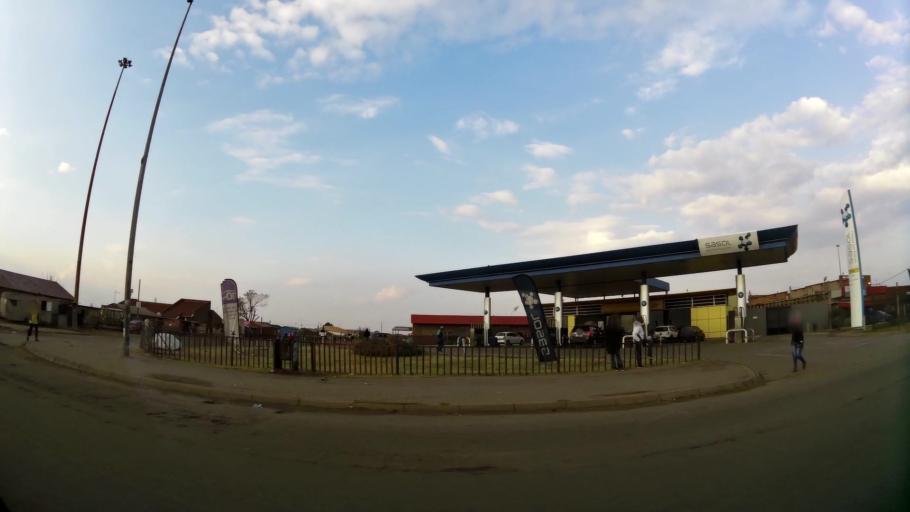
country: ZA
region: Gauteng
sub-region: City of Johannesburg Metropolitan Municipality
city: Orange Farm
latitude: -26.5805
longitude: 27.8425
